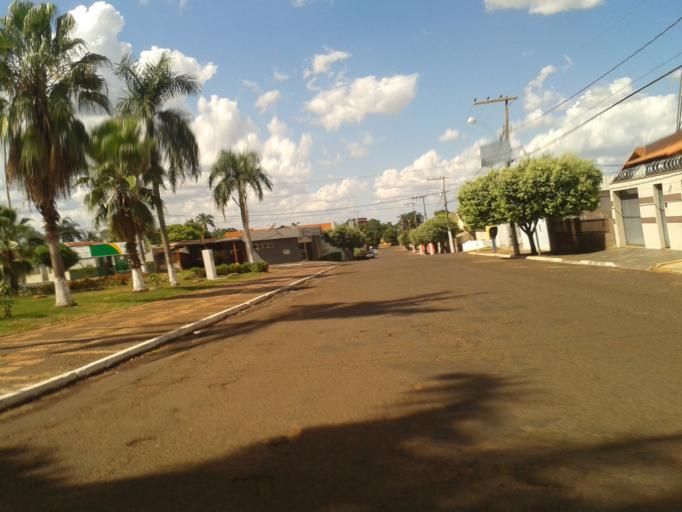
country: BR
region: Minas Gerais
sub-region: Santa Vitoria
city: Santa Vitoria
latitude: -18.6926
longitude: -49.9433
